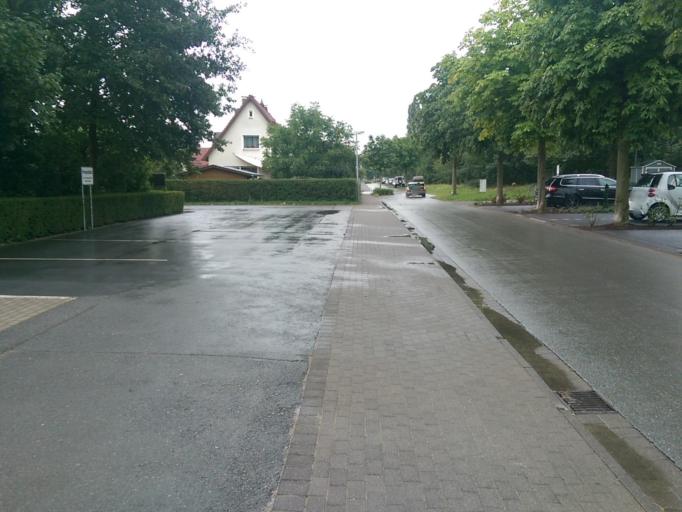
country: DE
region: North Rhine-Westphalia
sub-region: Regierungsbezirk Detmold
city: Guetersloh
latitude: 51.9057
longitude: 8.3515
